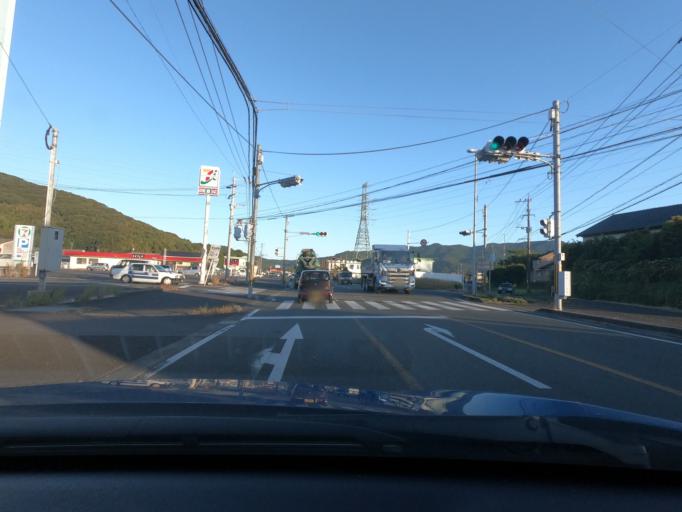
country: JP
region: Kagoshima
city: Satsumasendai
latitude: 31.8081
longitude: 130.3377
